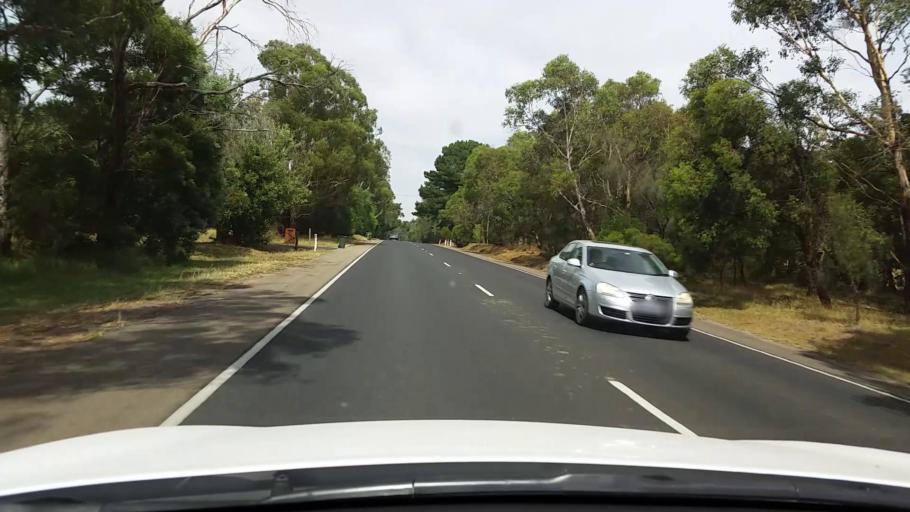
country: AU
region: Victoria
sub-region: Mornington Peninsula
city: Balnarring
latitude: -38.3481
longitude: 145.1633
